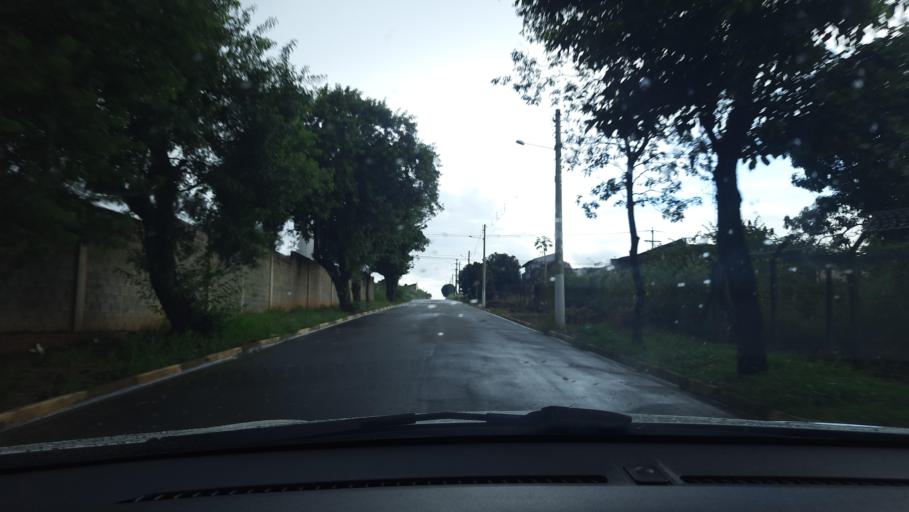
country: BR
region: Sao Paulo
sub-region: Casa Branca
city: Casa Branca
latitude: -21.7532
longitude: -47.0728
